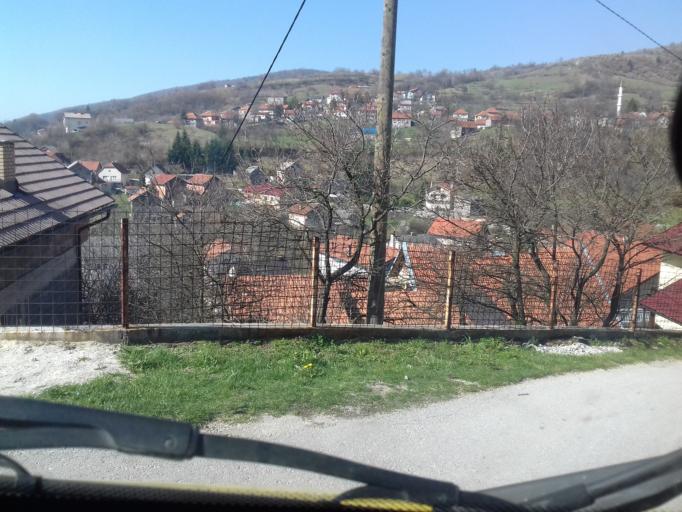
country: BA
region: Federation of Bosnia and Herzegovina
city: Travnik
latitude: 44.2452
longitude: 17.7242
